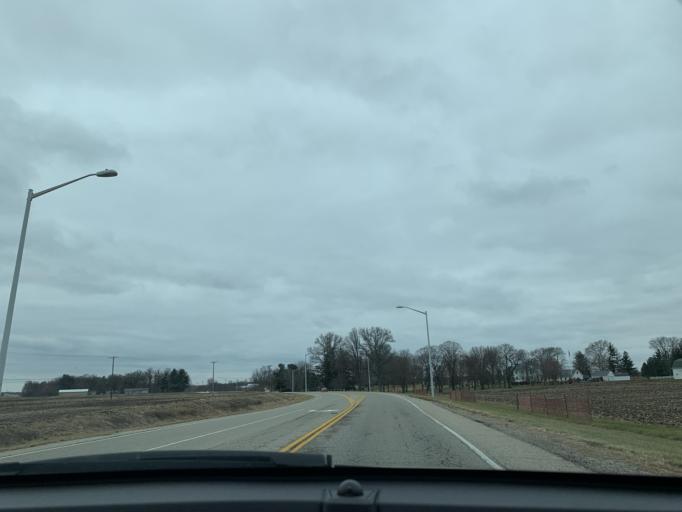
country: US
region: Illinois
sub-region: Sangamon County
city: Jerome
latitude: 39.7375
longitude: -89.6899
